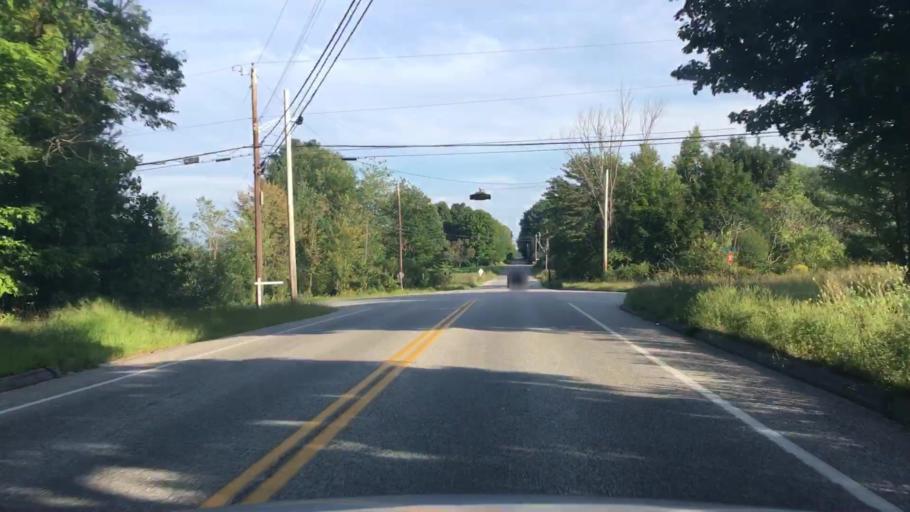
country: US
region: Maine
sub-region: Cumberland County
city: South Windham
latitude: 43.7384
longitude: -70.4185
